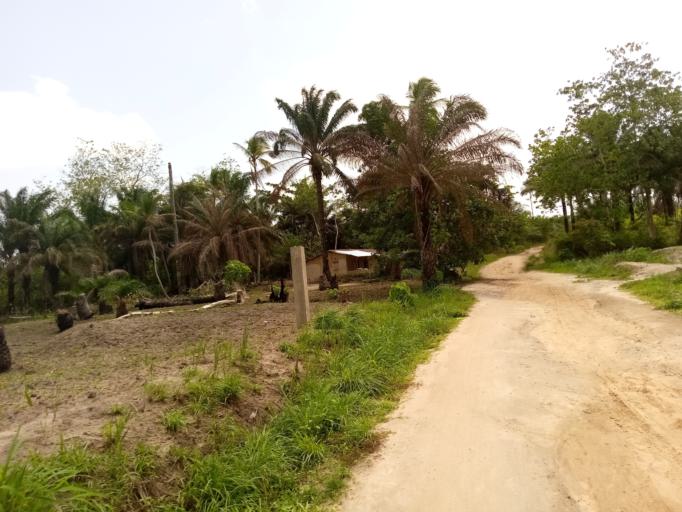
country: SL
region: Western Area
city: Waterloo
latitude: 8.3673
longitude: -13.0028
